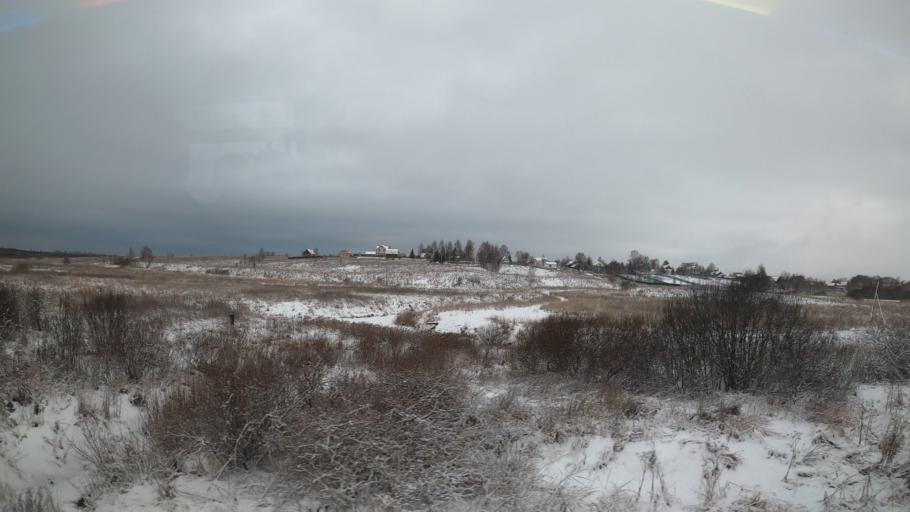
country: RU
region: Jaroslavl
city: Pereslavl'-Zalesskiy
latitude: 56.7012
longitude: 38.9127
